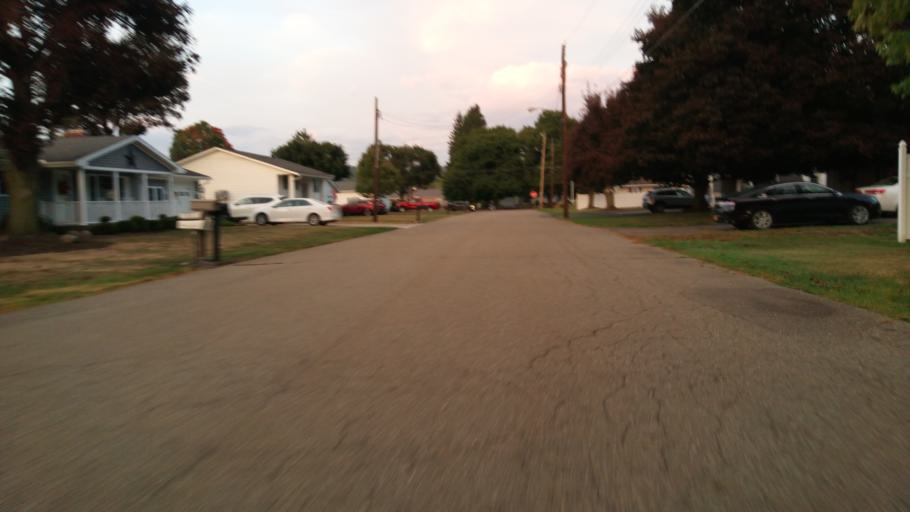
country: US
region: New York
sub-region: Chemung County
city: Southport
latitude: 42.0550
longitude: -76.7827
